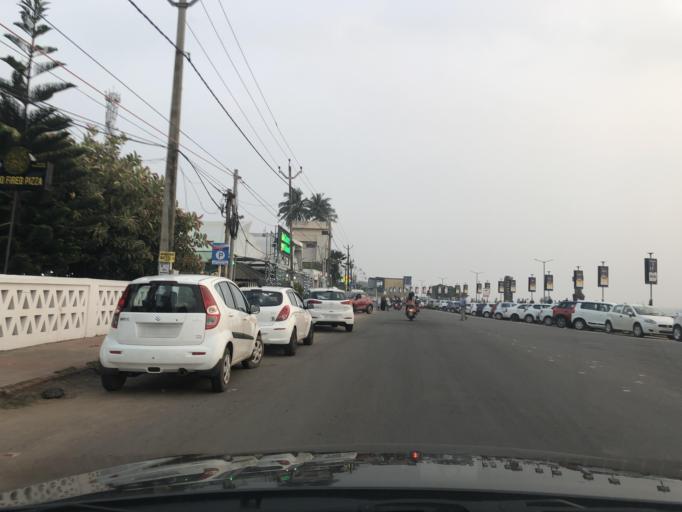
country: IN
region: Kerala
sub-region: Kozhikode
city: Kozhikode
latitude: 11.2527
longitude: 75.7710
